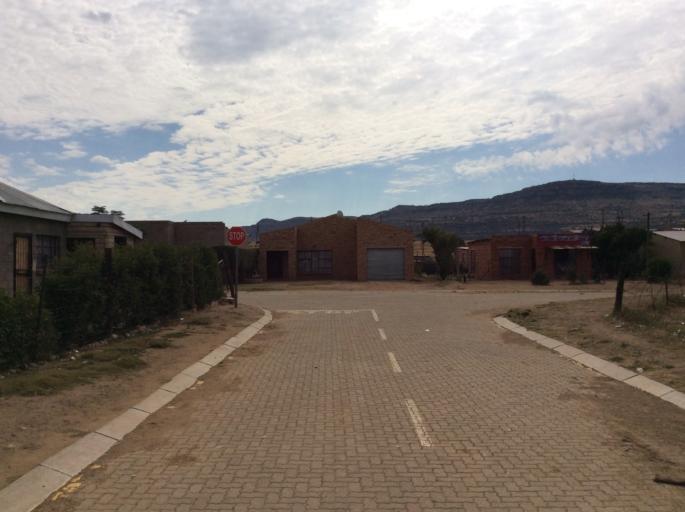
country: LS
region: Mafeteng
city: Mafeteng
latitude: -29.7219
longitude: 27.0100
